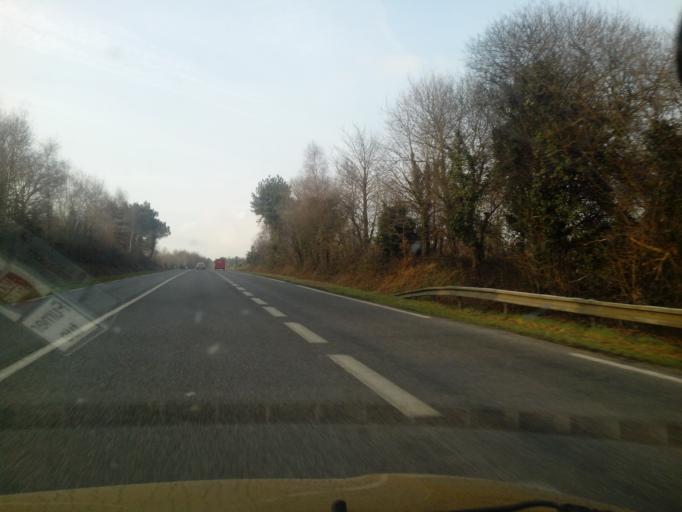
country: FR
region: Brittany
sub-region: Departement du Morbihan
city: Molac
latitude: 47.7270
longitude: -2.4411
